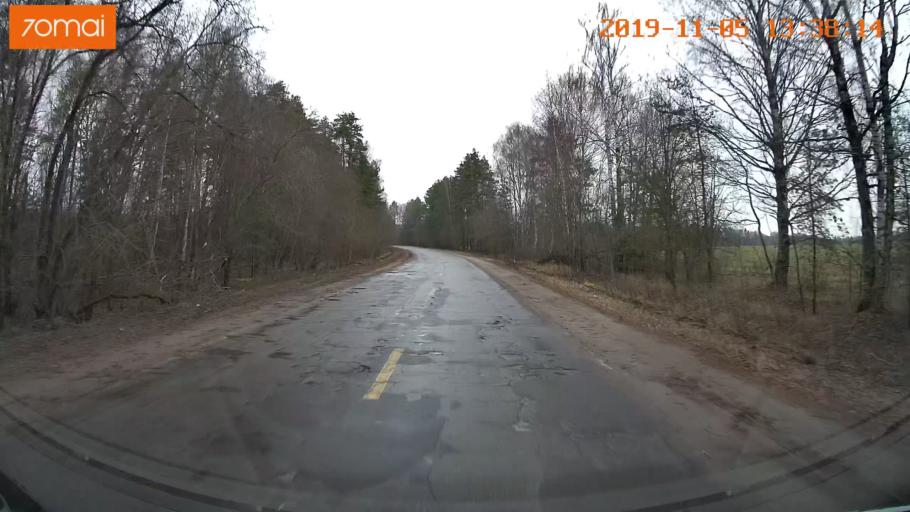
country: RU
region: Ivanovo
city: Shuya
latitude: 56.9300
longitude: 41.3852
